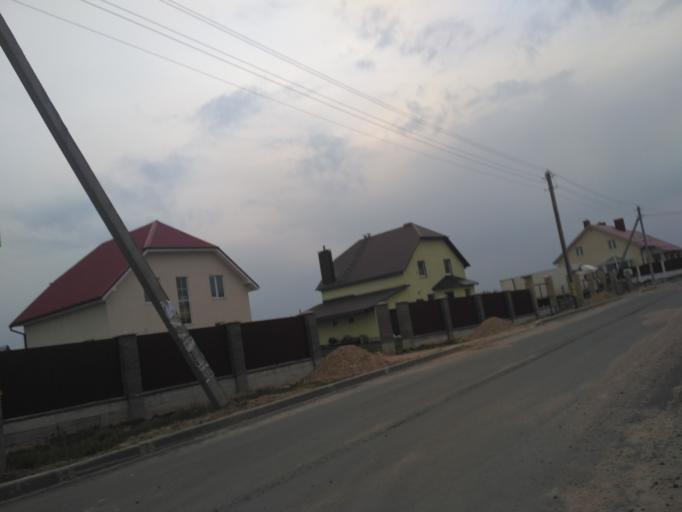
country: BY
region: Minsk
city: Slabada
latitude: 54.0055
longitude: 27.8725
